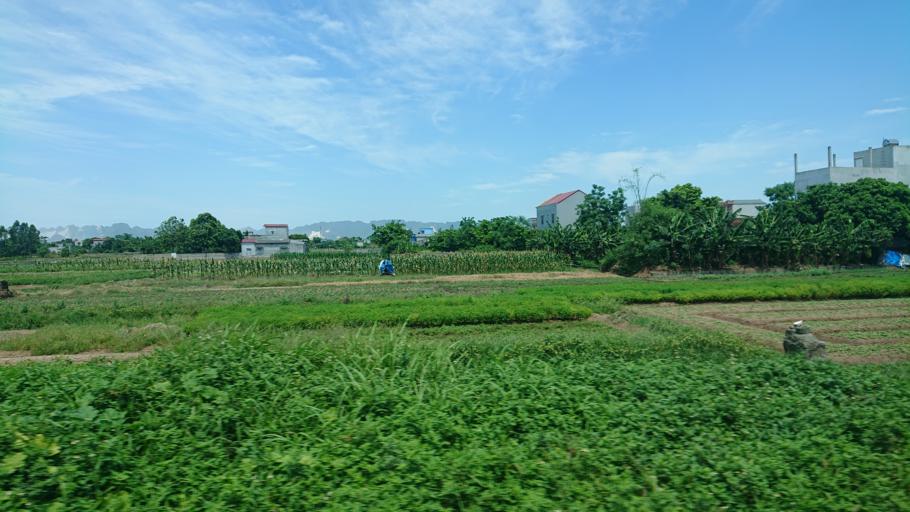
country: VN
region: Ha Nam
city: Thanh Pho Phu Ly
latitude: 20.5285
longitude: 105.9460
